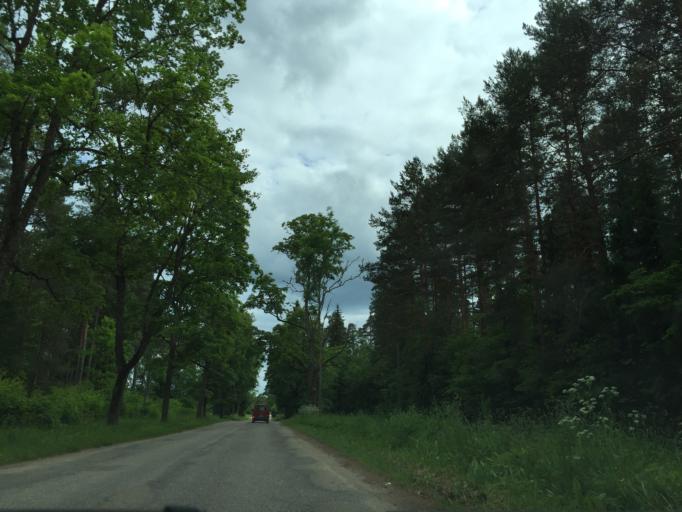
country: LV
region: Apes Novads
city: Ape
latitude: 57.5056
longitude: 26.3999
